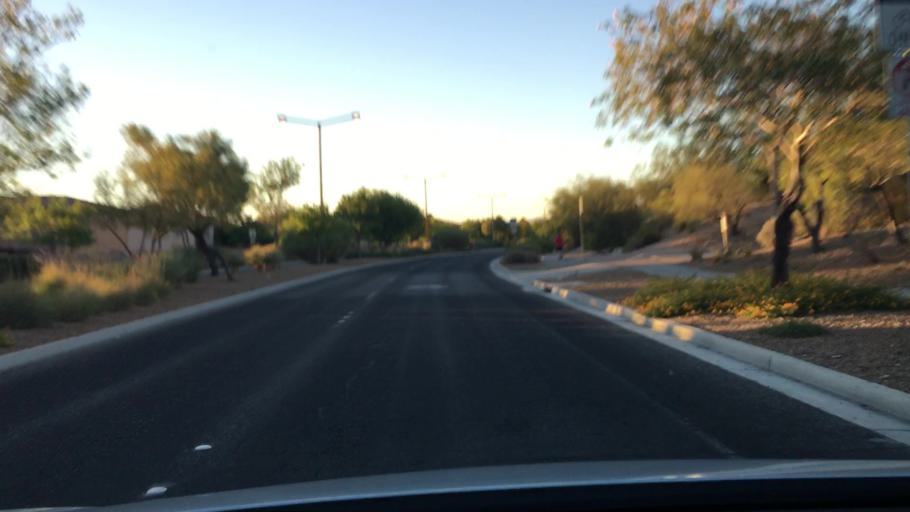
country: US
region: Nevada
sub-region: Clark County
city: Summerlin South
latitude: 36.1223
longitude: -115.3357
